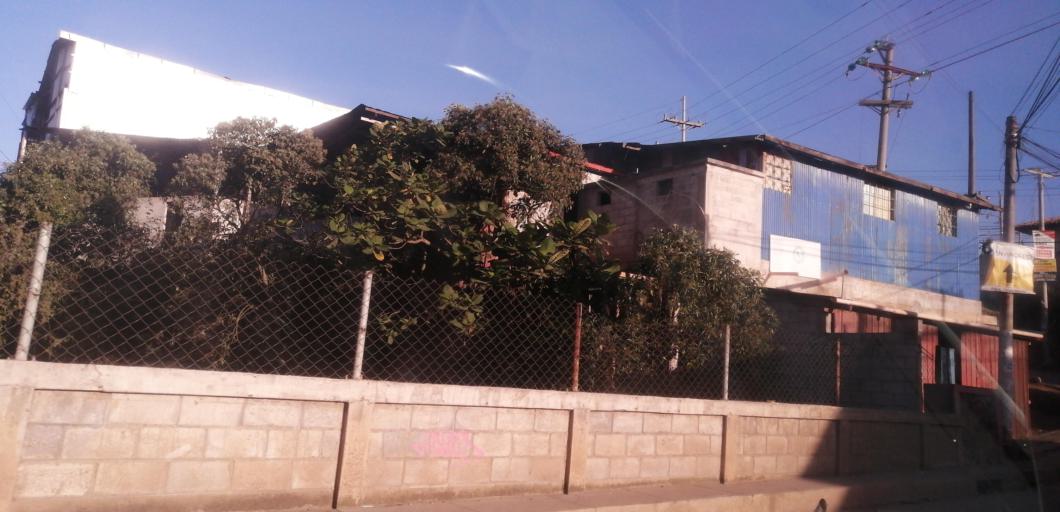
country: GT
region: Quetzaltenango
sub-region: Municipio de La Esperanza
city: La Esperanza
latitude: 14.8667
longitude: -91.5396
